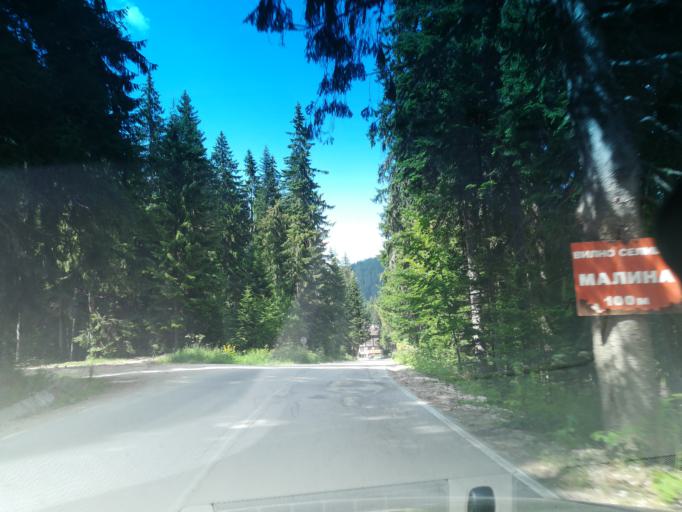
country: BG
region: Smolyan
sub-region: Obshtina Smolyan
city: Smolyan
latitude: 41.6514
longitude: 24.6849
